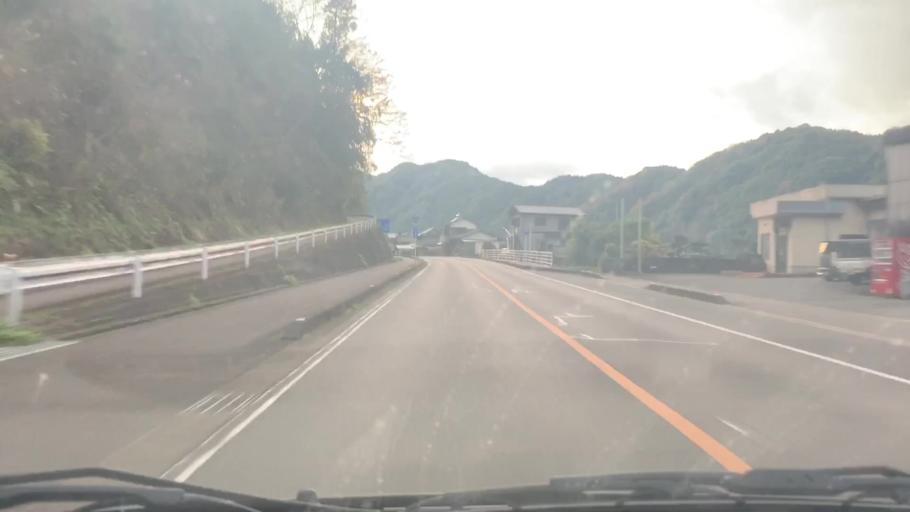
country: JP
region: Saga Prefecture
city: Kashima
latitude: 33.0857
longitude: 130.0771
